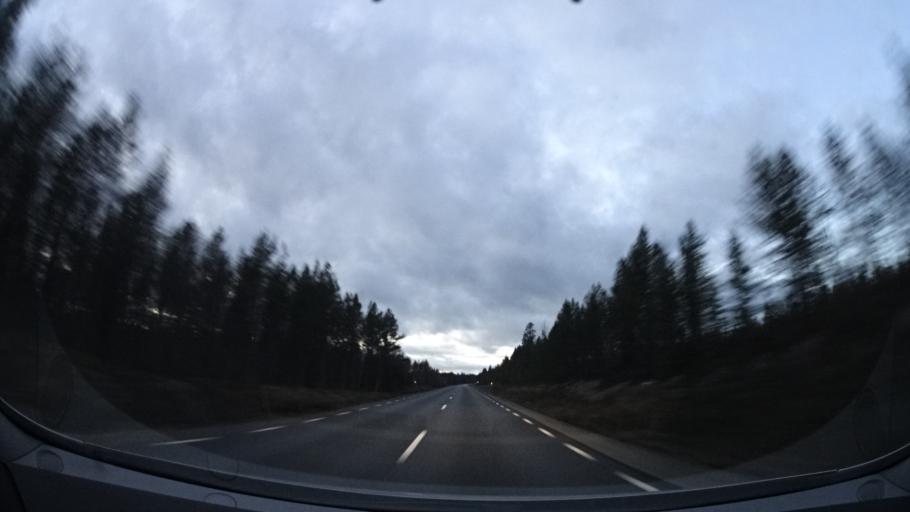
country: SE
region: Vaesterbotten
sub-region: Asele Kommun
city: Asele
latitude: 64.1842
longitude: 17.1985
